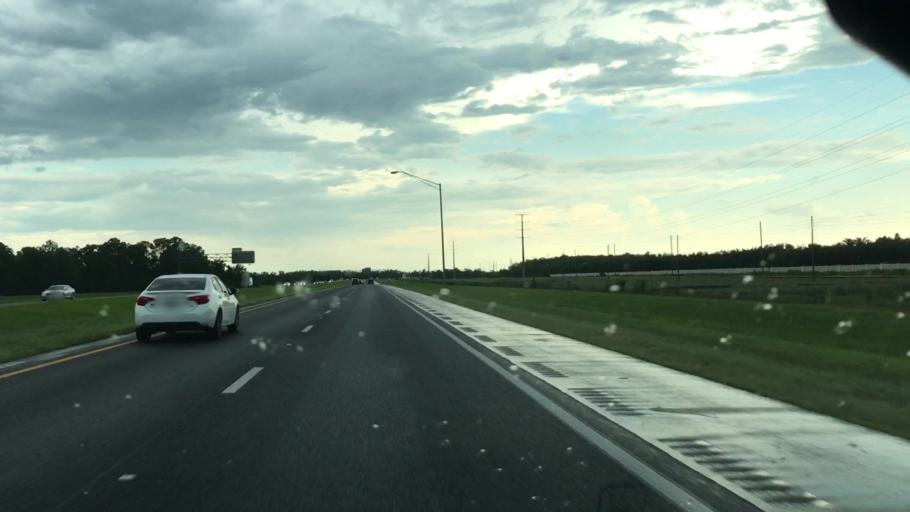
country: US
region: Florida
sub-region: Orange County
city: Meadow Woods
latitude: 28.3934
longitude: -81.2532
